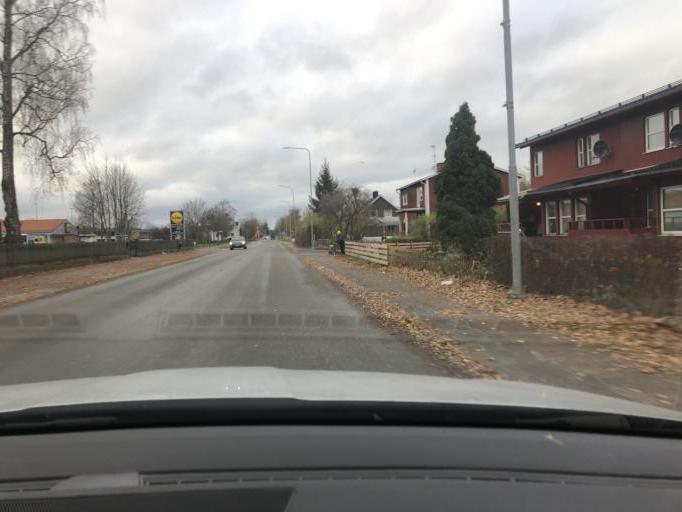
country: SE
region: Uppsala
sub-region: Tierps Kommun
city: Tierp
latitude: 60.3425
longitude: 17.5115
